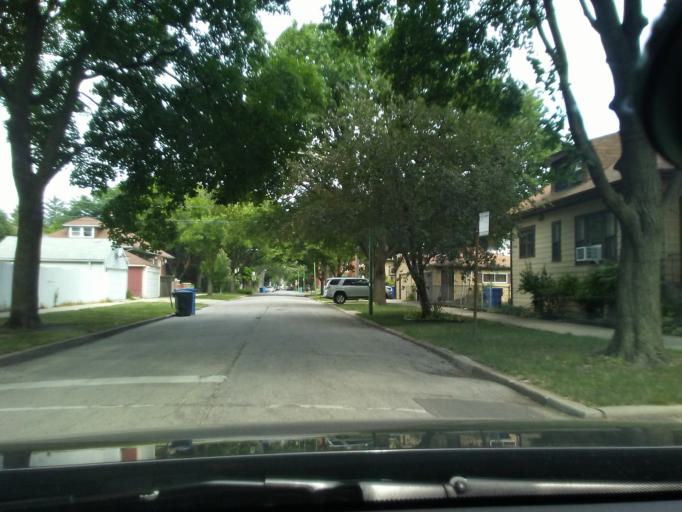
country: US
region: Illinois
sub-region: Cook County
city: Lincolnwood
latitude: 41.9663
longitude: -87.7439
